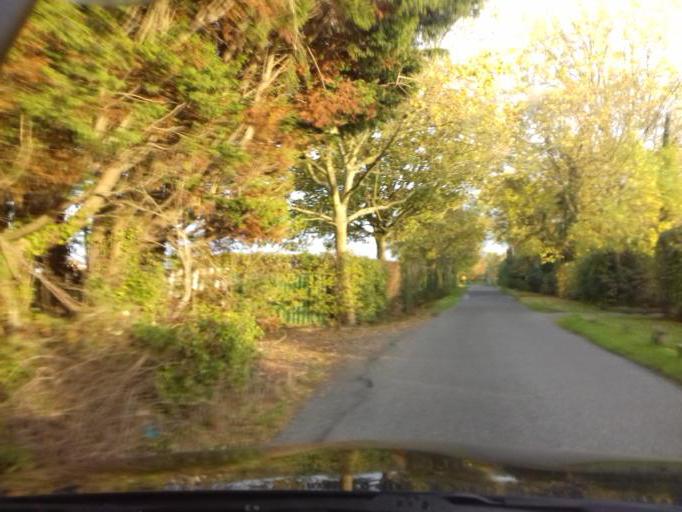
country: IE
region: Leinster
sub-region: An Mhi
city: Dunboyne
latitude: 53.3895
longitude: -6.4712
